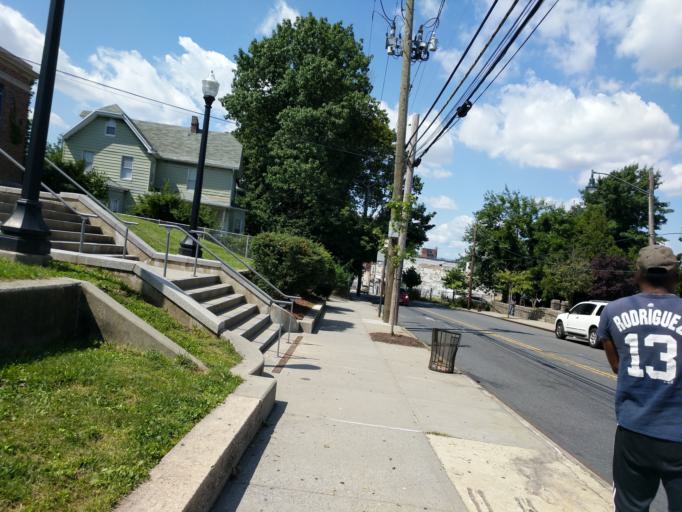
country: US
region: New Jersey
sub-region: Hudson County
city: Bayonne
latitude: 40.6347
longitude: -74.1147
